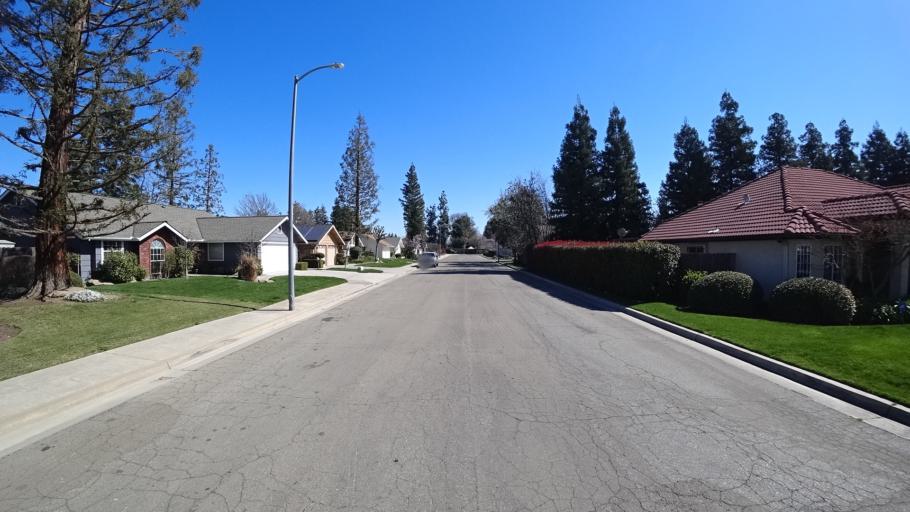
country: US
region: California
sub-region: Fresno County
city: Clovis
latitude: 36.8465
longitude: -119.7630
